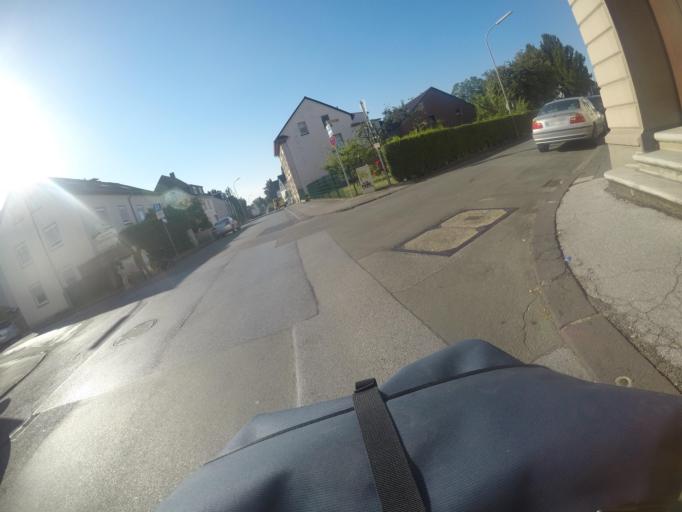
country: DE
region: North Rhine-Westphalia
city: Haan
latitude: 51.1924
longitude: 7.0140
